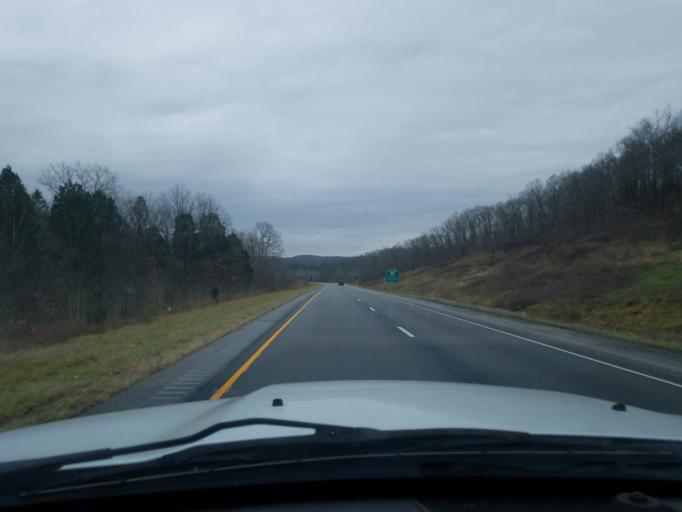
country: US
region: Indiana
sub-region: Dubois County
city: Ferdinand
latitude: 38.2311
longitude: -86.6844
